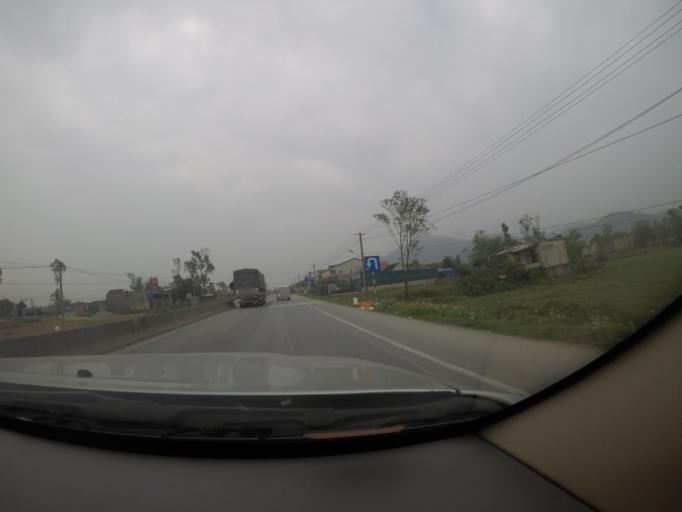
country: VN
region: Ha Tinh
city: Ky Anh
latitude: 18.1453
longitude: 106.2487
